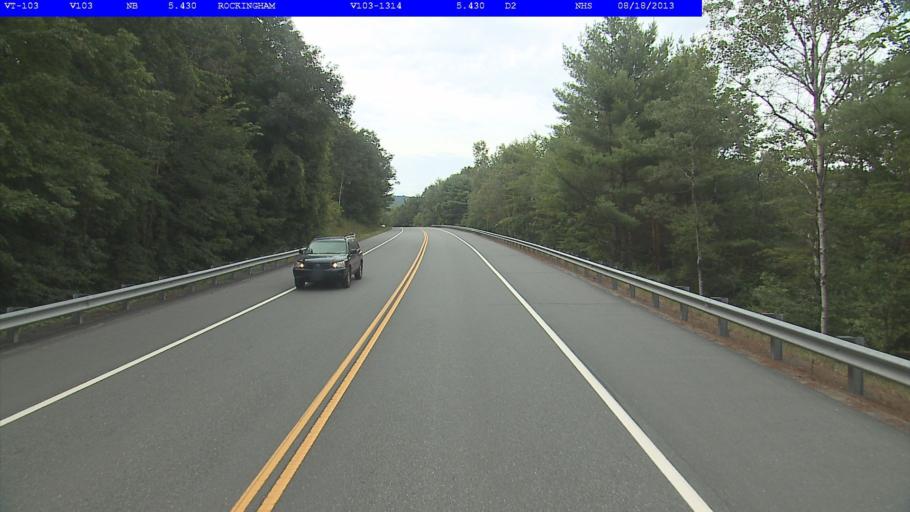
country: US
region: Vermont
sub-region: Windham County
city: Rockingham
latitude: 43.2199
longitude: -72.5380
